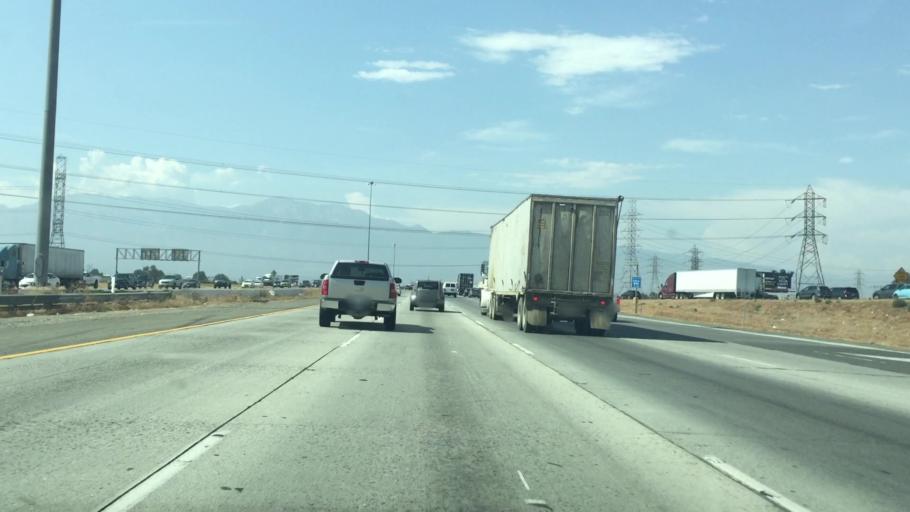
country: US
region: California
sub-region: Riverside County
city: Mira Loma
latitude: 34.0250
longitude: -117.5501
